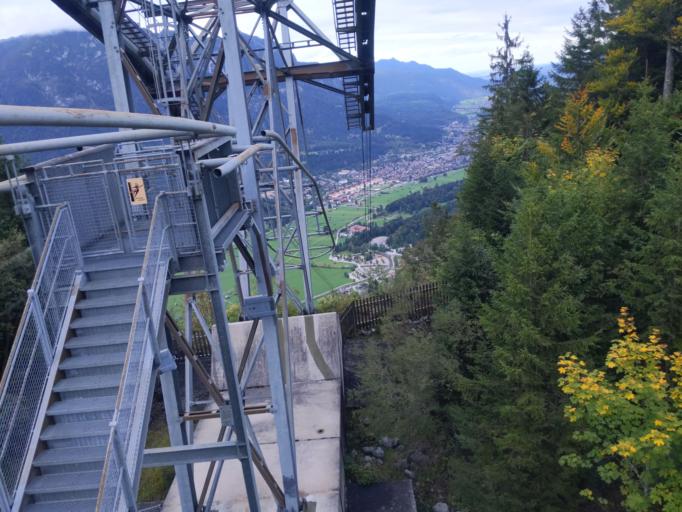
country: DE
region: Bavaria
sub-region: Upper Bavaria
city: Grainau
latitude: 47.4597
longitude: 11.0576
